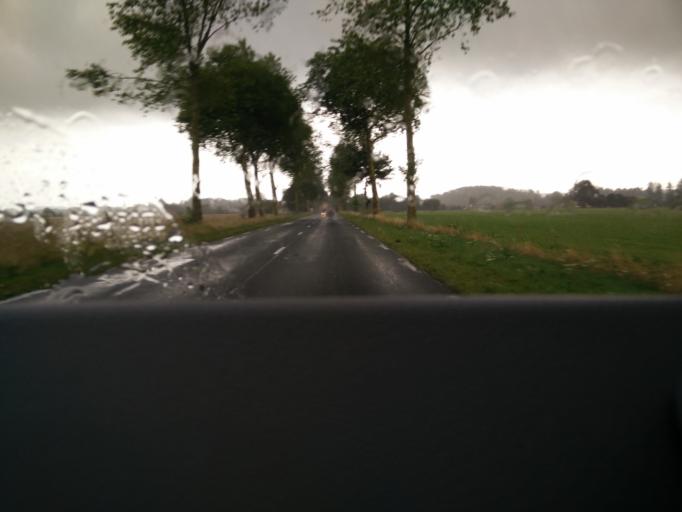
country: FR
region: Nord-Pas-de-Calais
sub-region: Departement du Pas-de-Calais
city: Savy-Berlette
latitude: 50.3492
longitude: 2.5385
